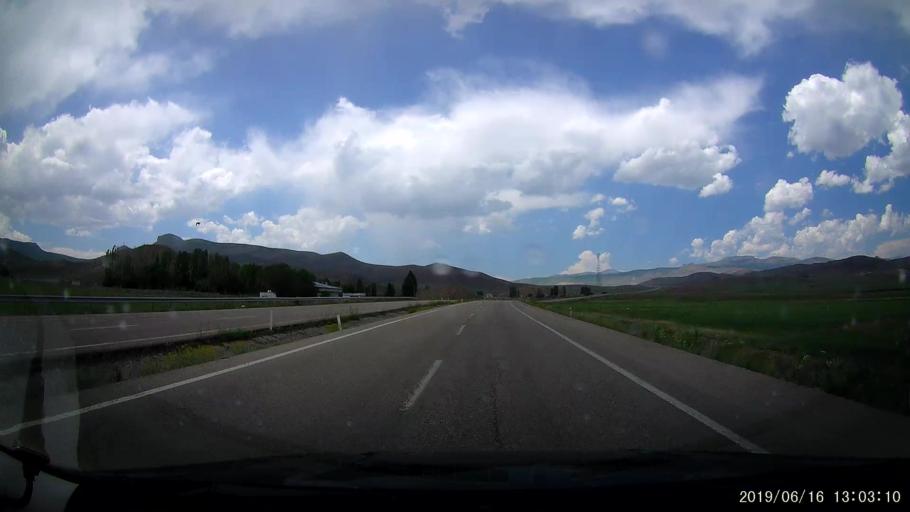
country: TR
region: Agri
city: Sulucem
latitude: 39.5789
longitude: 43.7965
